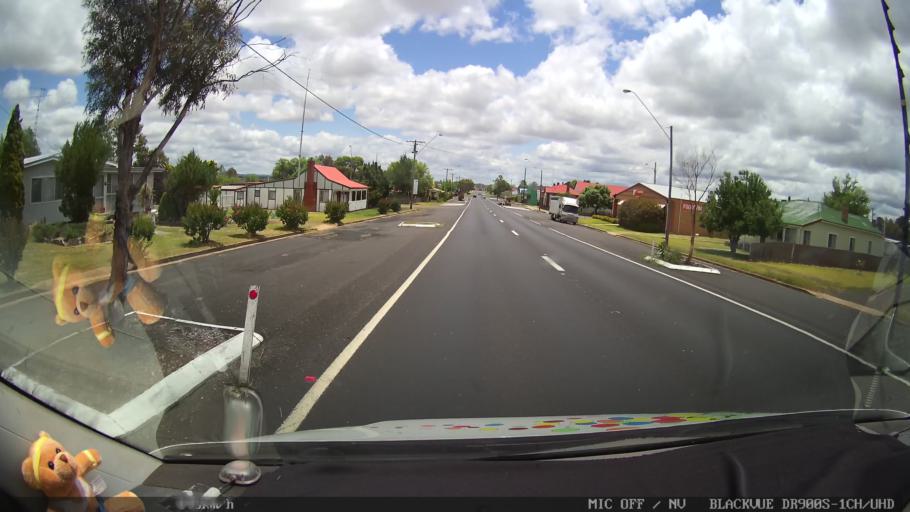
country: AU
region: New South Wales
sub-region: Glen Innes Severn
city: Glen Innes
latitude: -29.4415
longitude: 151.8463
